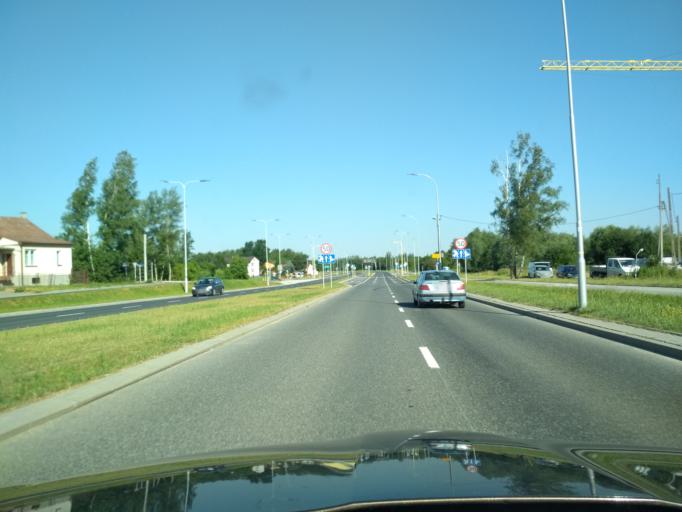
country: PL
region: Subcarpathian Voivodeship
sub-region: Rzeszow
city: Rzeszow
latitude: 50.0640
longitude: 22.0034
